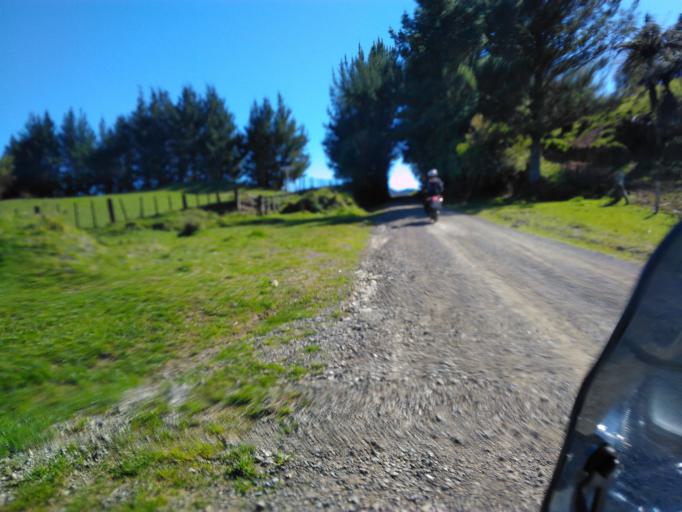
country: NZ
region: Bay of Plenty
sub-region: Opotiki District
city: Opotiki
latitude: -38.3663
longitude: 177.5981
